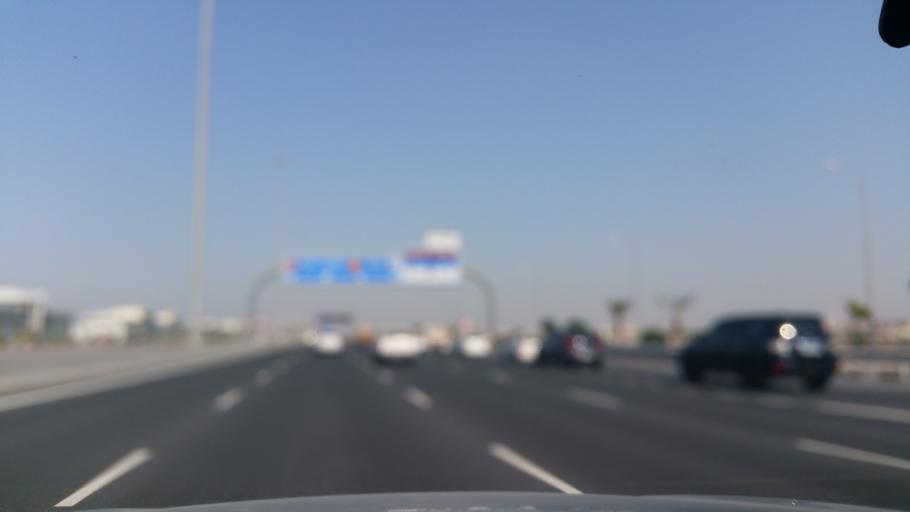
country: QA
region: Al Wakrah
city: Al Wukayr
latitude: 25.2032
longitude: 51.4809
